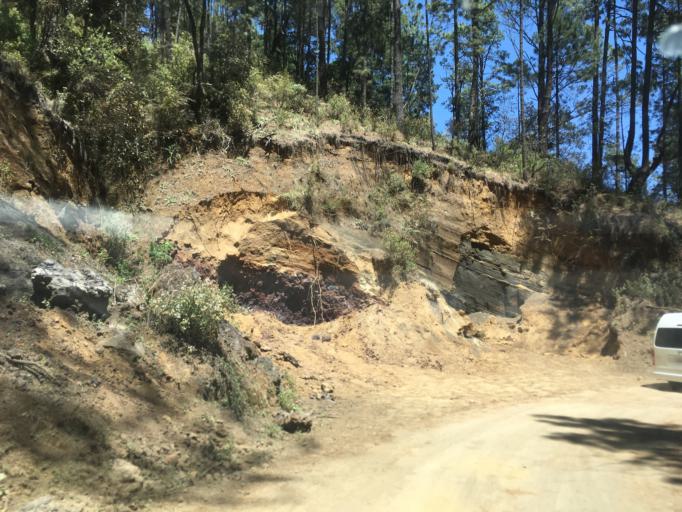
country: MX
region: Michoacan
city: Angahuan
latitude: 19.4711
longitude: -102.2409
